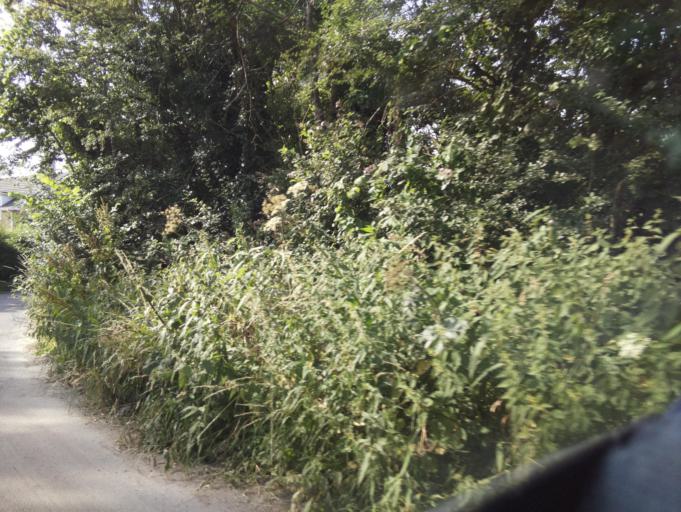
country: GB
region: England
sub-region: Wiltshire
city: Minety
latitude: 51.6223
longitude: -1.9690
